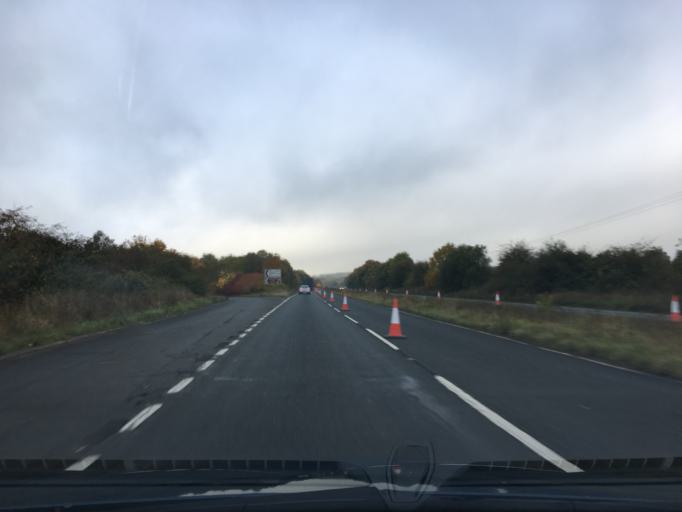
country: GB
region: England
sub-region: Hampshire
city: Alton
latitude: 51.1372
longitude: -0.9735
